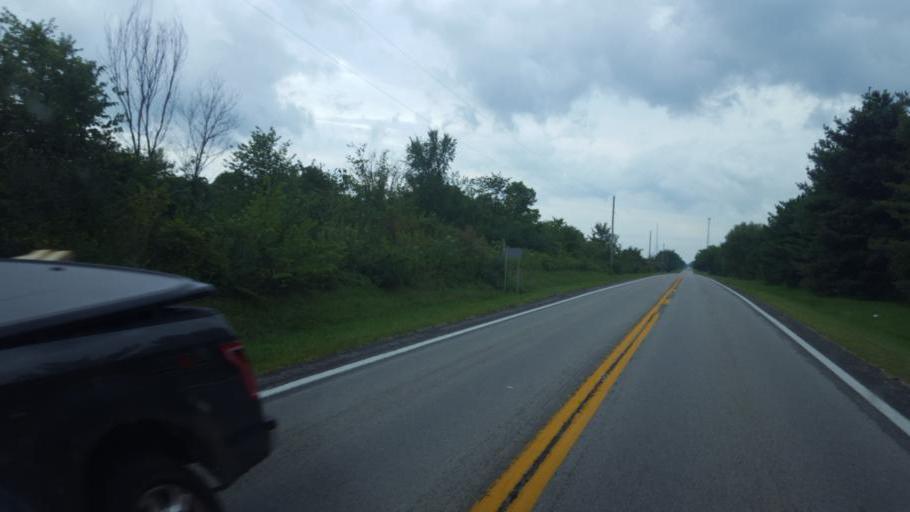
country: US
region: Ohio
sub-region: Delaware County
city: Ashley
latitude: 40.3559
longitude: -82.9902
